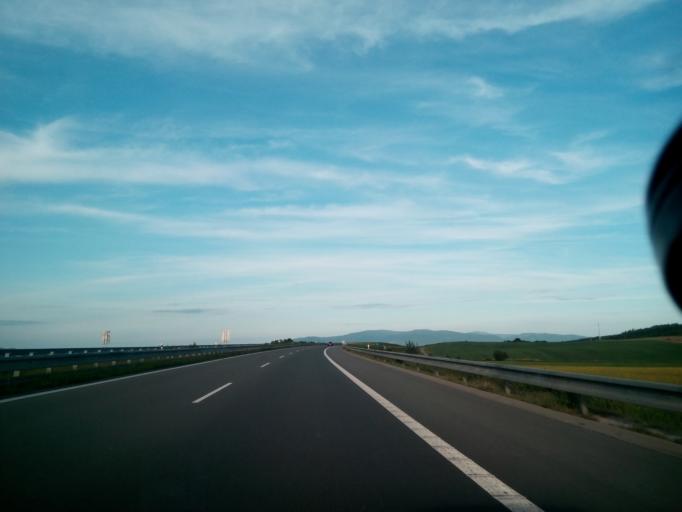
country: SK
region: Presovsky
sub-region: Okres Presov
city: Presov
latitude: 49.0078
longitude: 21.1344
